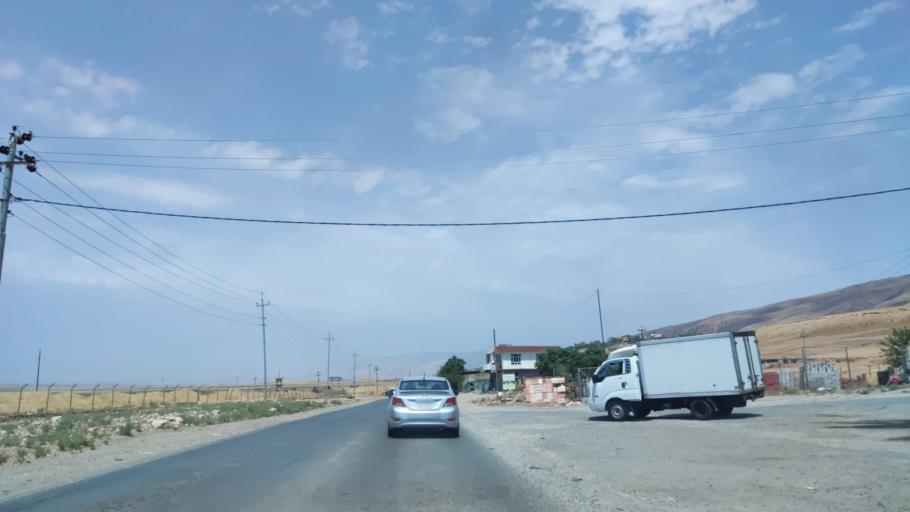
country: IQ
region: Arbil
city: Shaqlawah
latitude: 36.5295
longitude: 44.3590
